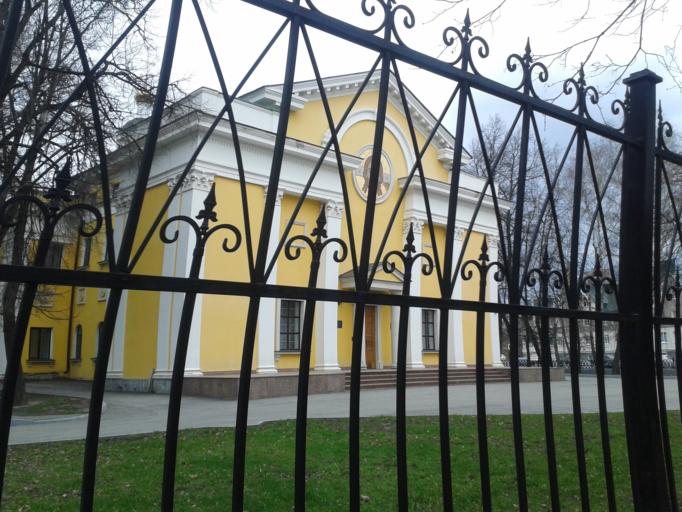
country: RU
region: Rjazan
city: Ryazan'
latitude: 54.6344
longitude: 39.7462
